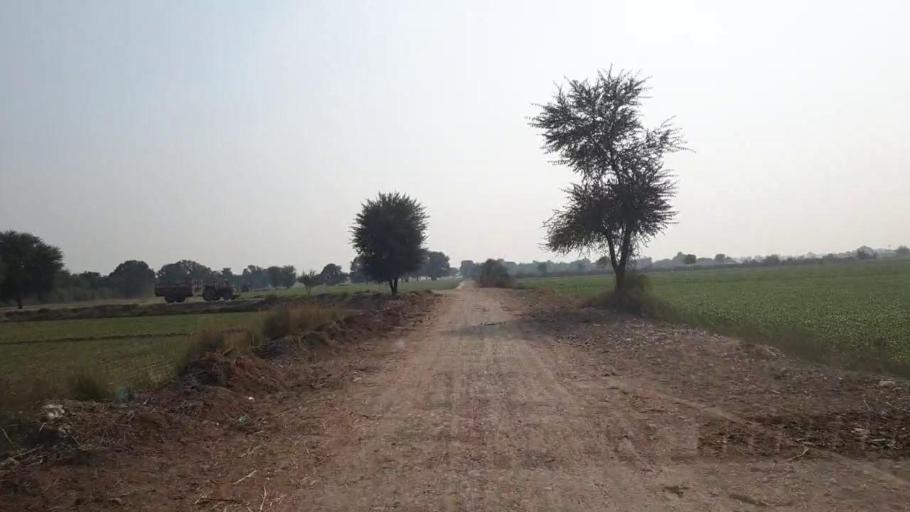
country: PK
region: Sindh
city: Hala
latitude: 25.8308
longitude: 68.4478
